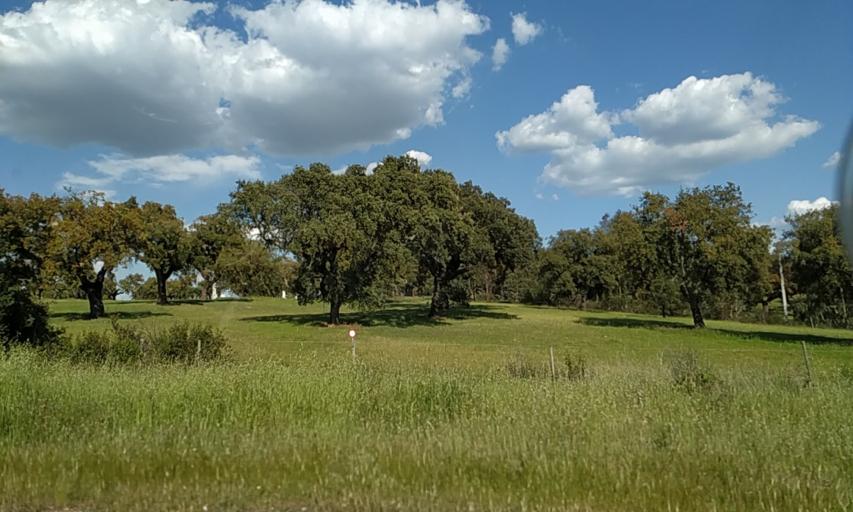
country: PT
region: Evora
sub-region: Estremoz
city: Estremoz
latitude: 38.8825
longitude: -7.5585
